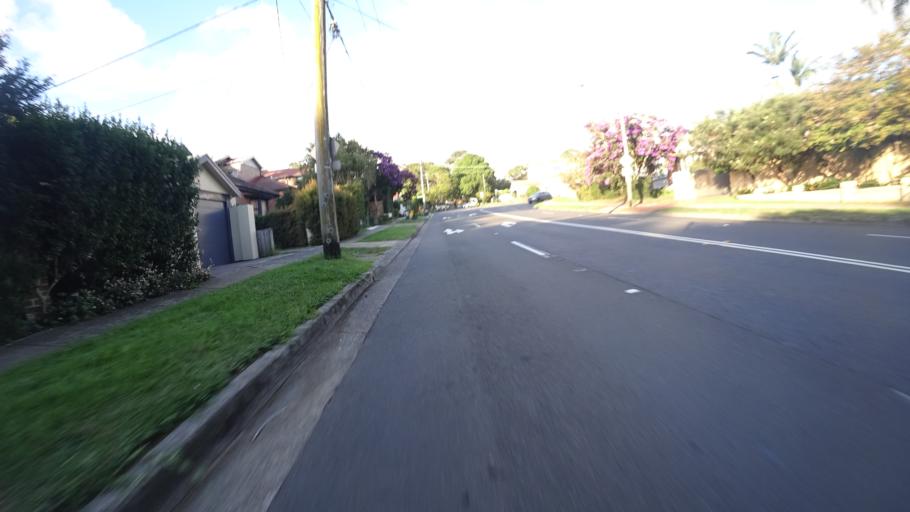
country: AU
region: New South Wales
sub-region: Lane Cove
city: Lane Cove
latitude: -33.8167
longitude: 151.1603
